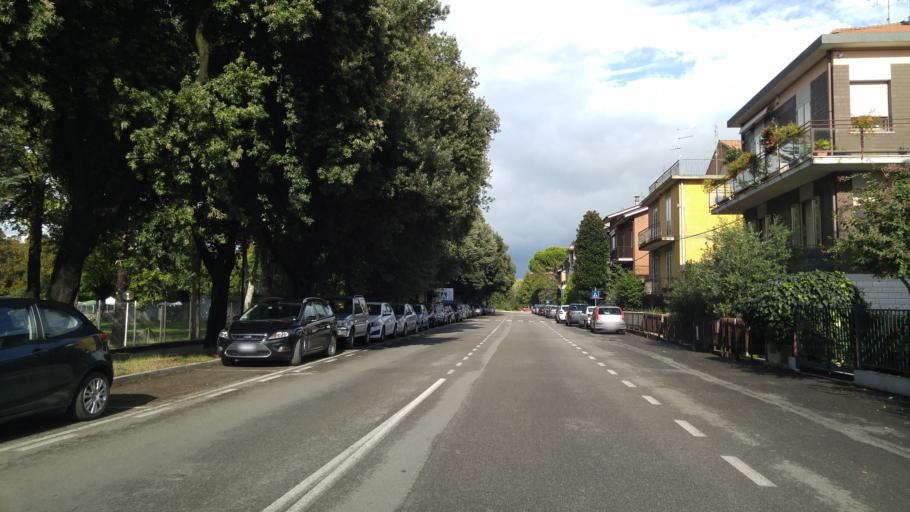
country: IT
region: The Marches
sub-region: Provincia di Pesaro e Urbino
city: Pesaro
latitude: 43.9026
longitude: 12.8949
